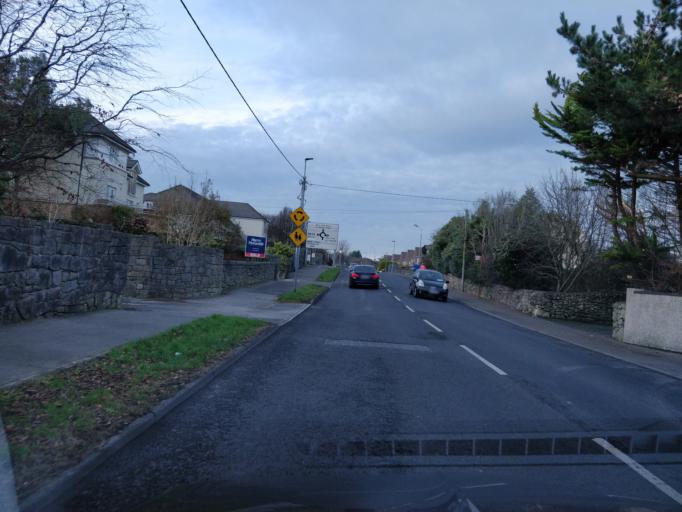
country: IE
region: Connaught
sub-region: County Galway
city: Bearna
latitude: 53.2667
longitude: -9.1065
